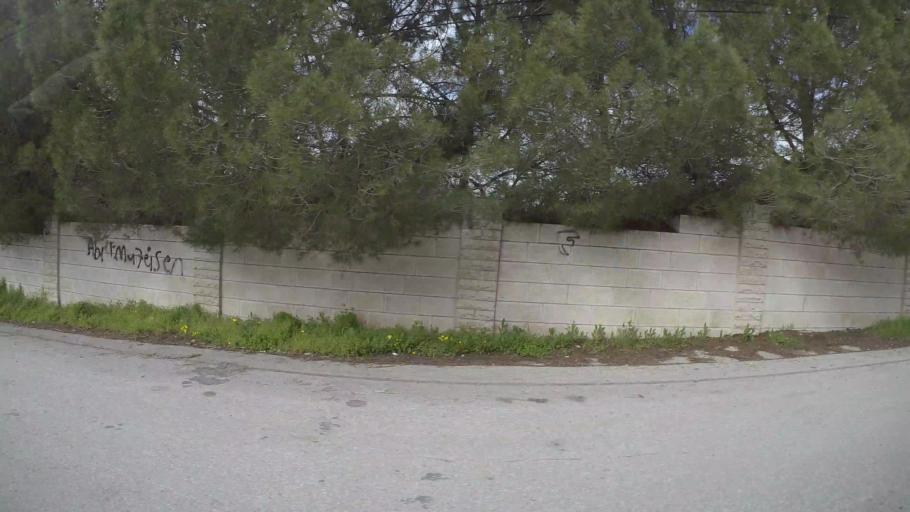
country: JO
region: Amman
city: Al Jubayhah
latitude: 32.0051
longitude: 35.8393
